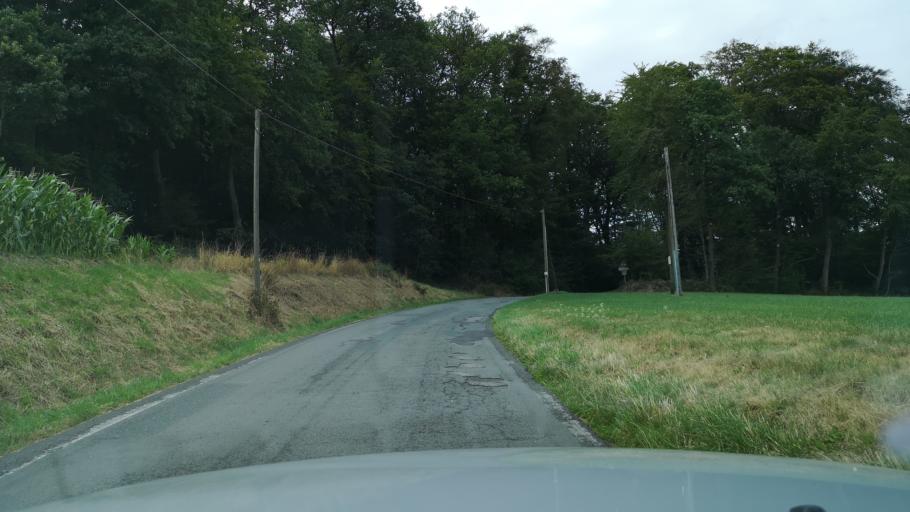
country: DE
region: North Rhine-Westphalia
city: Sprockhovel
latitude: 51.3434
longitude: 7.2015
